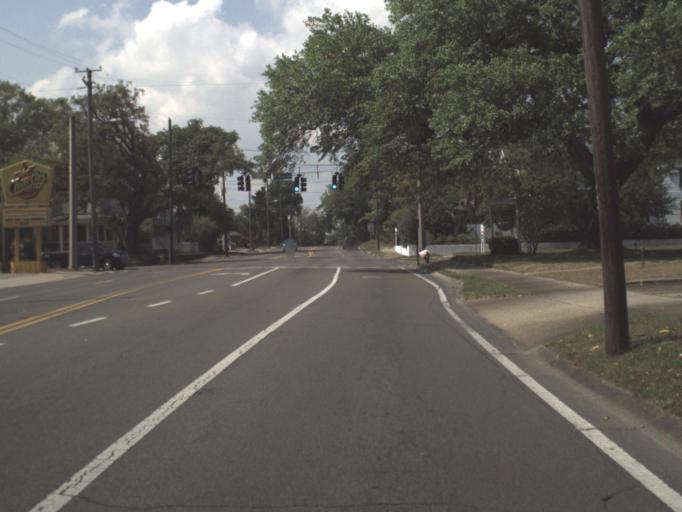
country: US
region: Florida
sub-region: Escambia County
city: Pensacola
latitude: 30.4291
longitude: -87.2084
